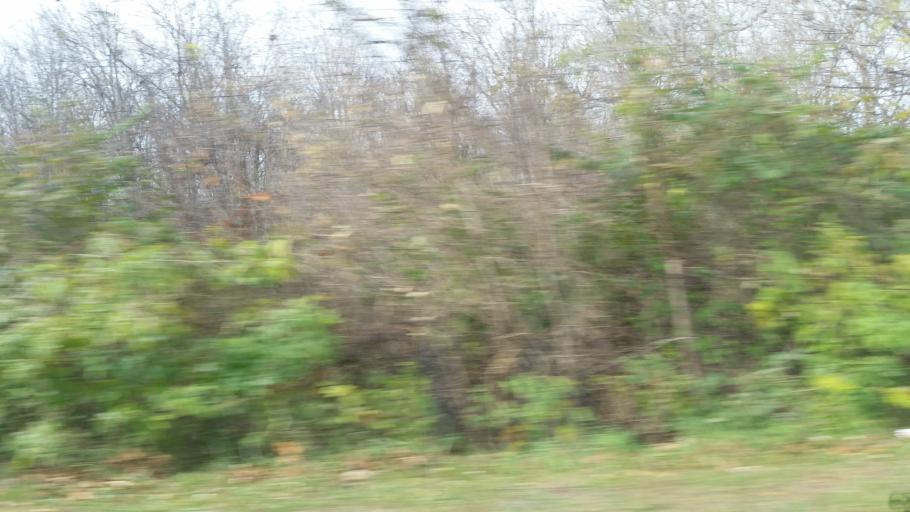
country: US
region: Indiana
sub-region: Howard County
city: Indian Heights
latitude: 40.4362
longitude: -86.1652
